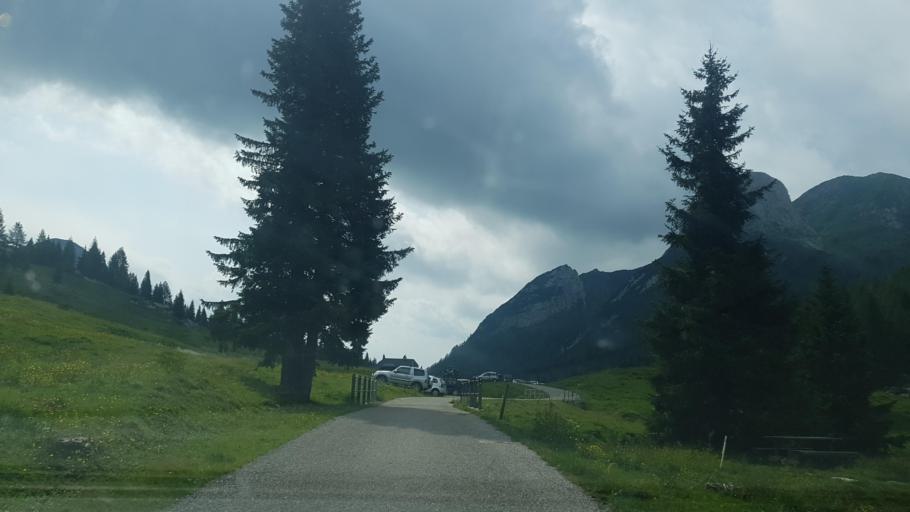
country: IT
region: Friuli Venezia Giulia
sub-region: Provincia di Udine
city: Paularo
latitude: 46.5677
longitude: 13.1696
